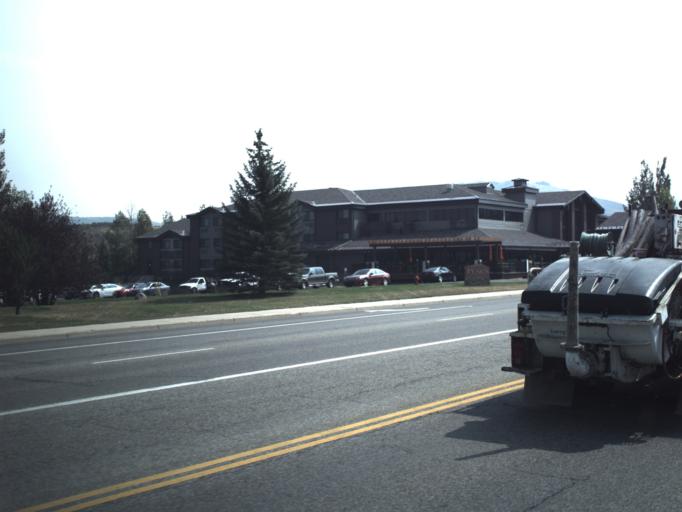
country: US
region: Utah
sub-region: Summit County
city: Park City
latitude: 40.6678
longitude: -111.5153
